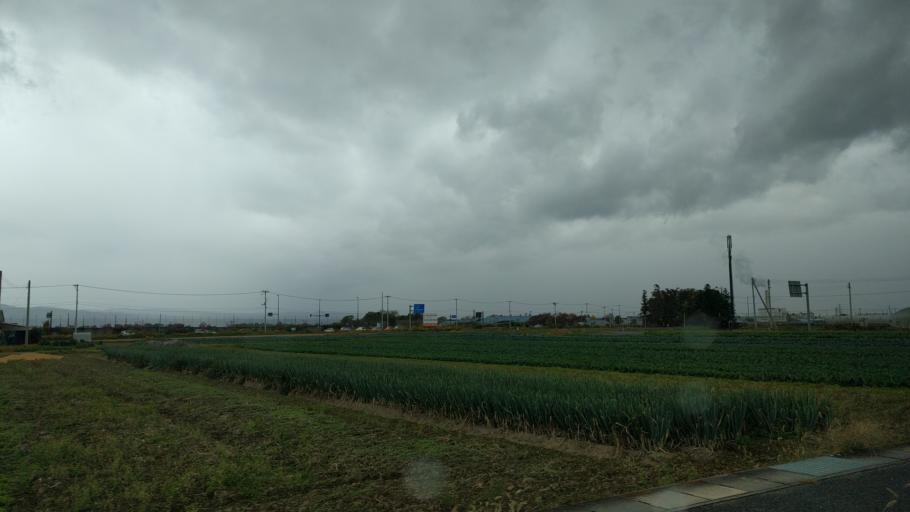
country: JP
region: Fukushima
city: Kitakata
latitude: 37.4852
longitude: 139.9029
